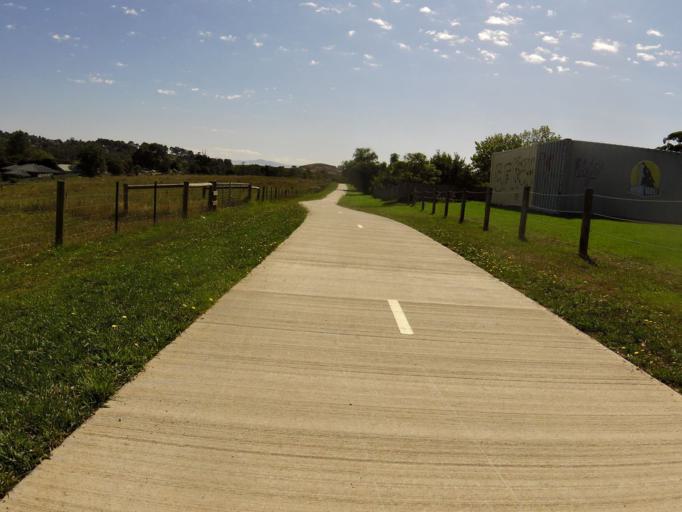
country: AU
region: Victoria
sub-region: Yarra Ranges
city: Kilsyth
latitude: -37.7813
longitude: 145.3278
